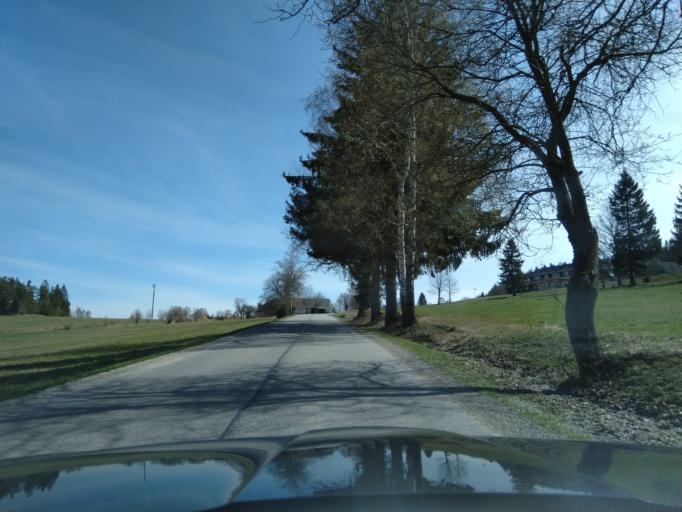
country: CZ
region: Jihocesky
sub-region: Okres Prachatice
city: Stachy
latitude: 49.0750
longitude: 13.6483
